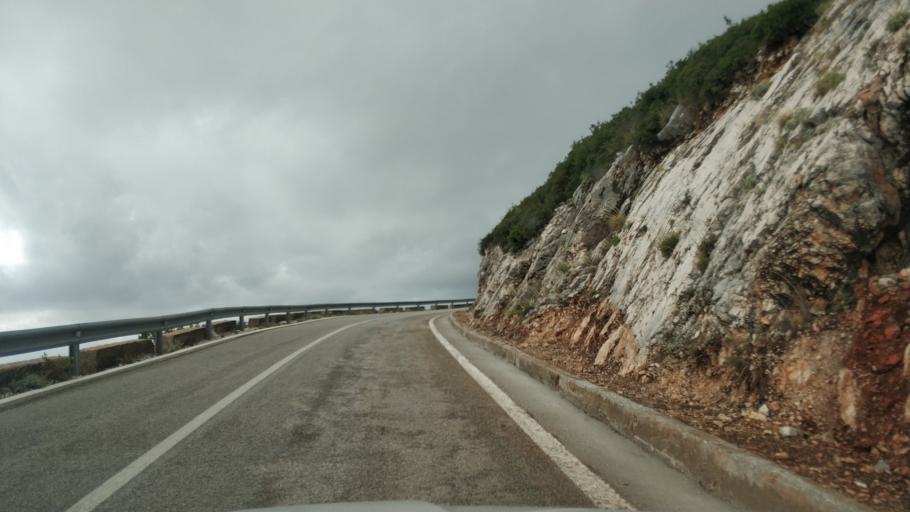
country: AL
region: Vlore
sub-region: Rrethi i Vlores
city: Vranisht
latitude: 40.1823
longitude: 19.6007
